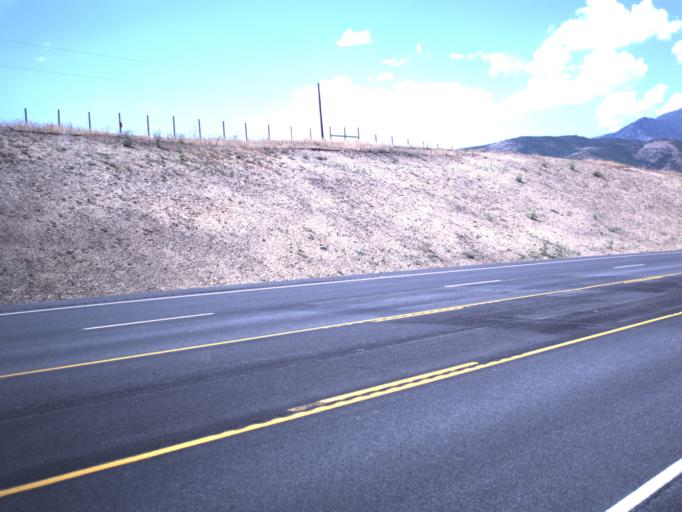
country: US
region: Utah
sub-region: Wasatch County
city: Midway
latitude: 40.4184
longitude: -111.4885
